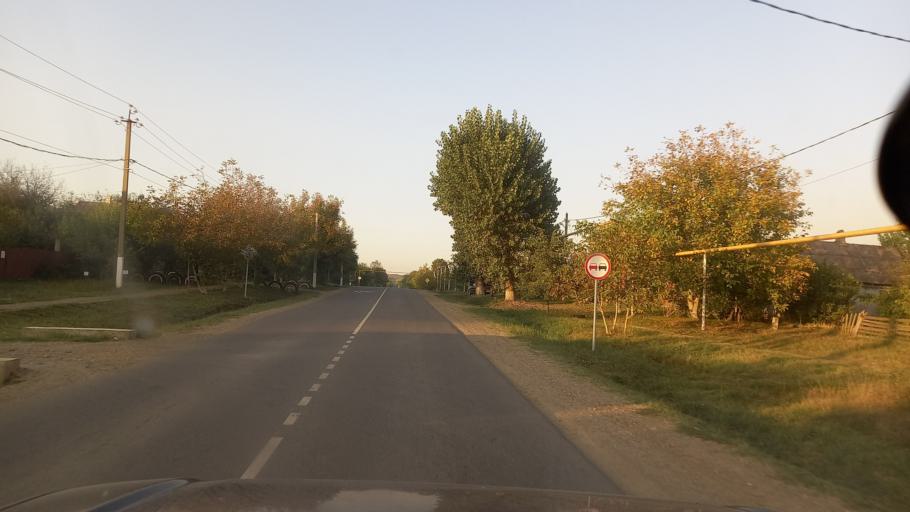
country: RU
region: Krasnodarskiy
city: Smolenskaya
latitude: 44.7698
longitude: 38.7824
